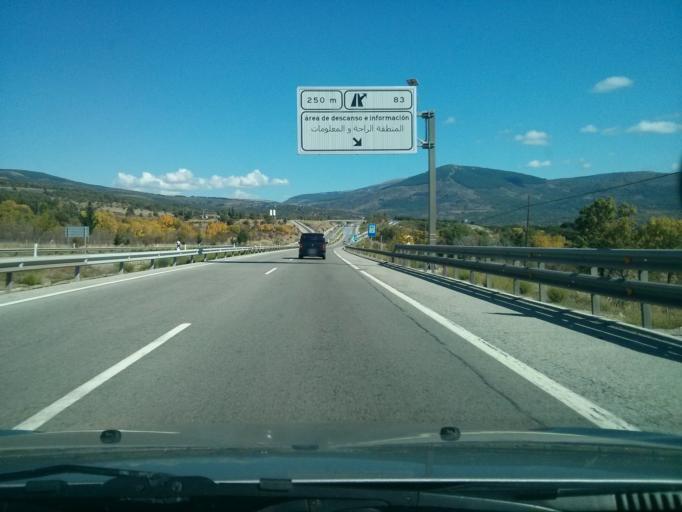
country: ES
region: Madrid
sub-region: Provincia de Madrid
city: Horcajo de la Sierra
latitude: 41.0557
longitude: -3.6136
